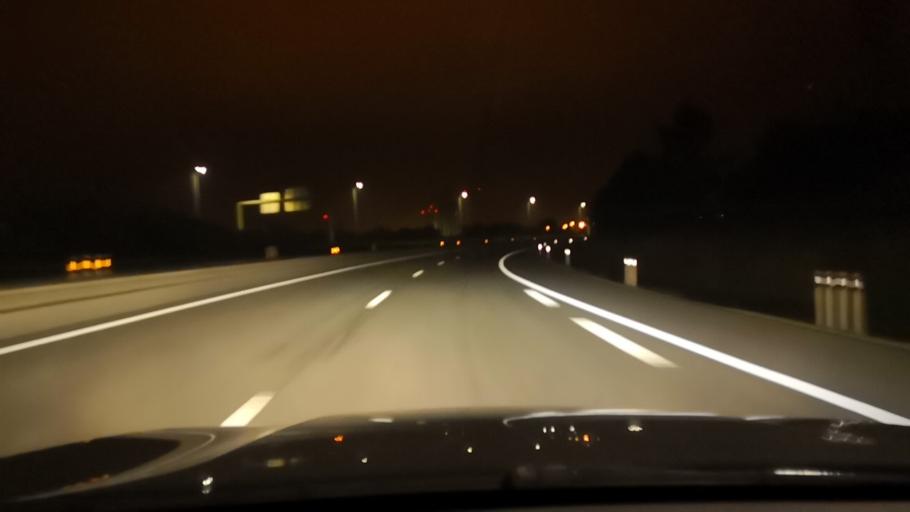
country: PT
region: Setubal
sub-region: Palmela
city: Palmela
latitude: 38.5794
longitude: -8.8633
